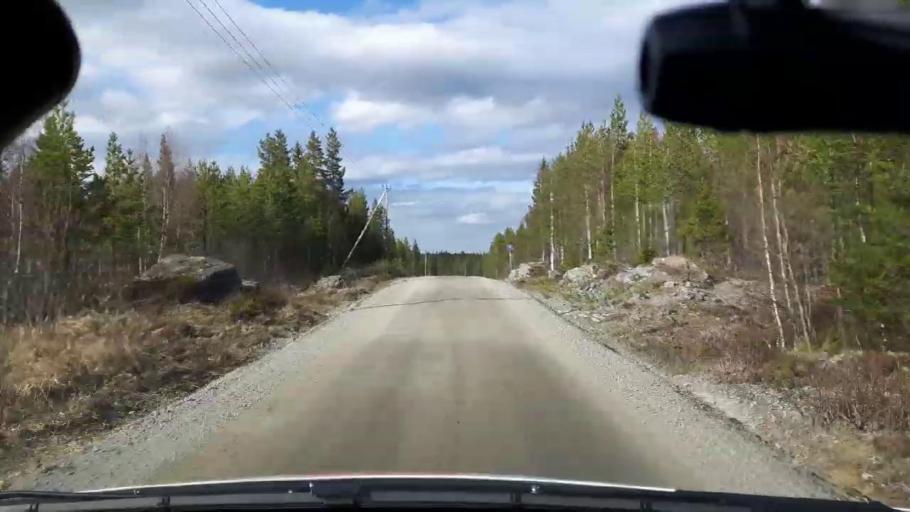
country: SE
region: Jaemtland
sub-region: Bergs Kommun
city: Hoverberg
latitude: 62.8694
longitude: 14.6640
